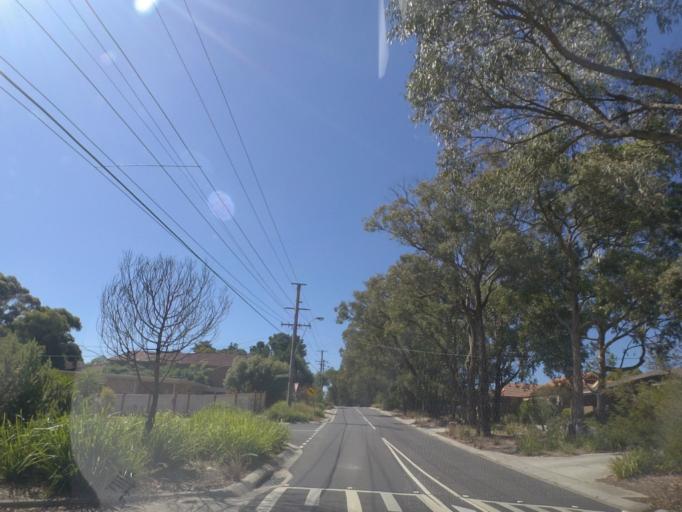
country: AU
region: Victoria
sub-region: Maroondah
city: Warranwood
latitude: -37.7701
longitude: 145.2505
